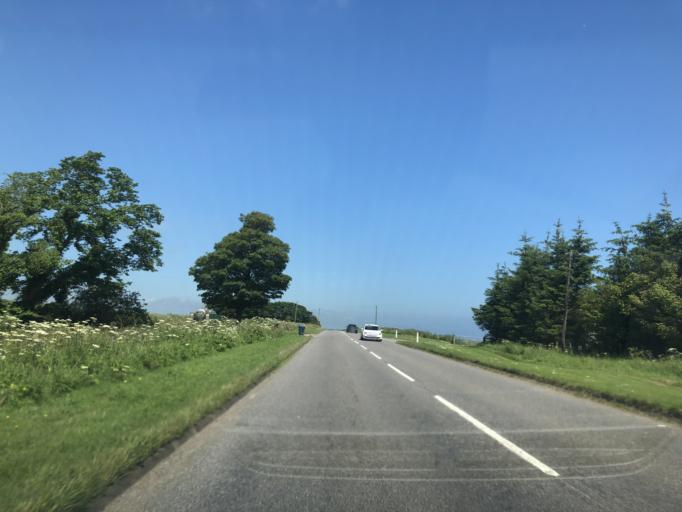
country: GB
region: Scotland
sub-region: Aberdeenshire
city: Stonehaven
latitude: 56.9340
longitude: -2.2078
